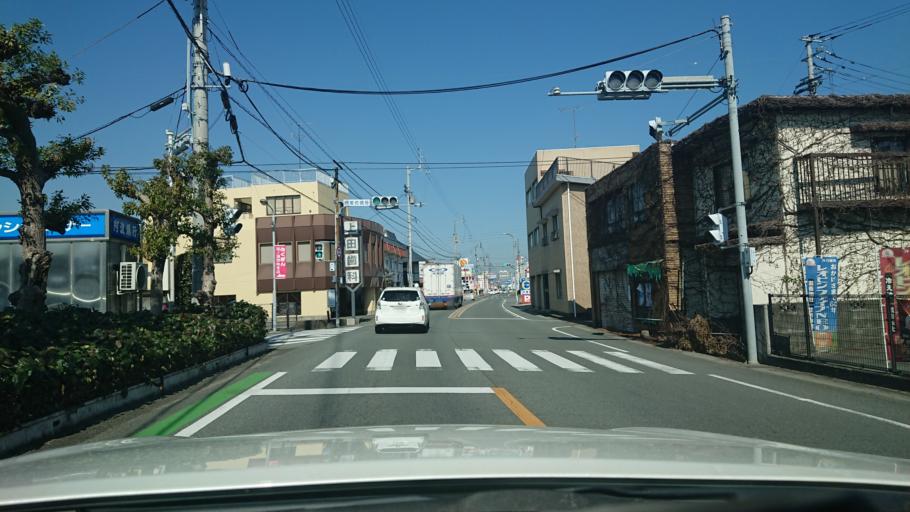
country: JP
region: Tokushima
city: Komatsushimacho
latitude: 33.9635
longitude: 134.6204
